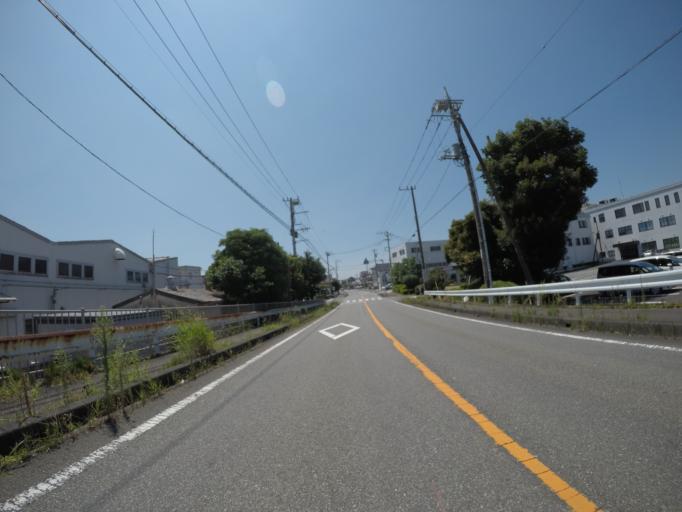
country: JP
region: Shizuoka
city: Fuji
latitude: 35.1622
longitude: 138.6649
